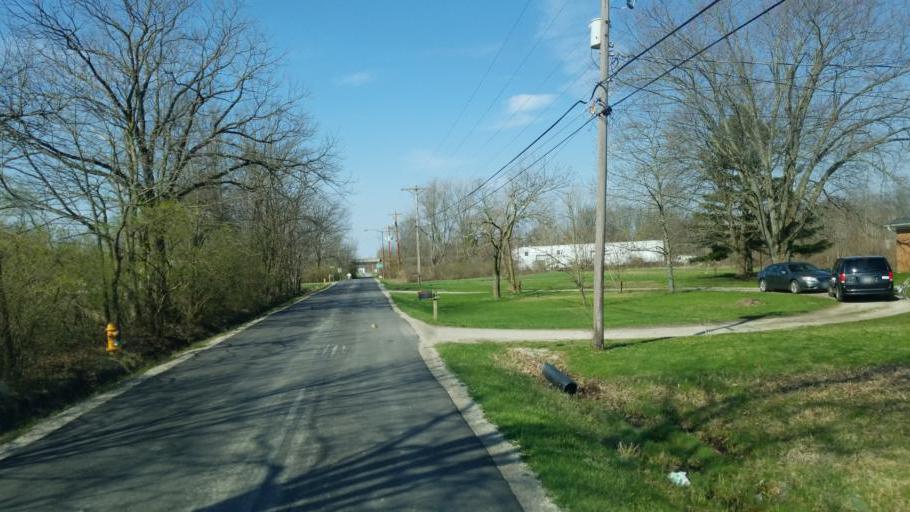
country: US
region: Ohio
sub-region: Delaware County
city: Delaware
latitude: 40.3054
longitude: -83.0453
